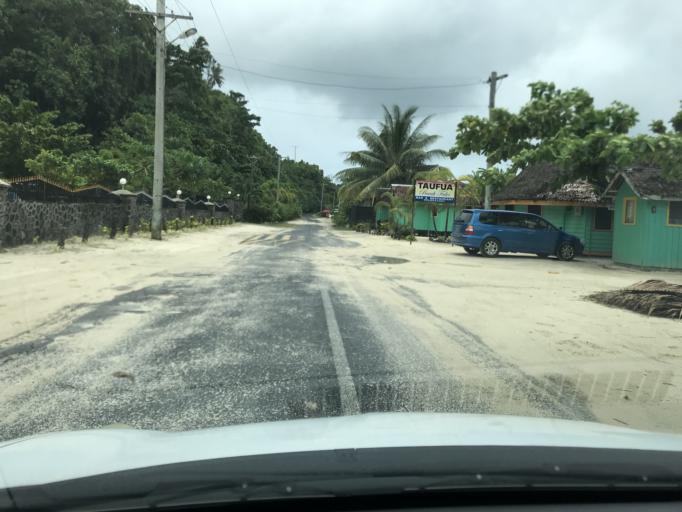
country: WS
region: Va`a-o-Fonoti
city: Samamea
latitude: -14.0459
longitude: -171.4460
